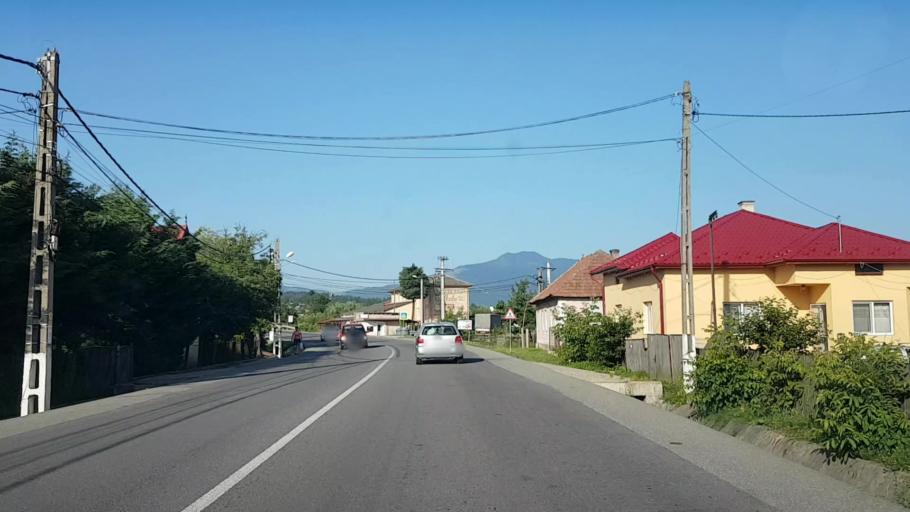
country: RO
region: Bistrita-Nasaud
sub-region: Comuna Prundu Bargaului
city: Susenii Bargaului
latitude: 47.2190
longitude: 24.7178
